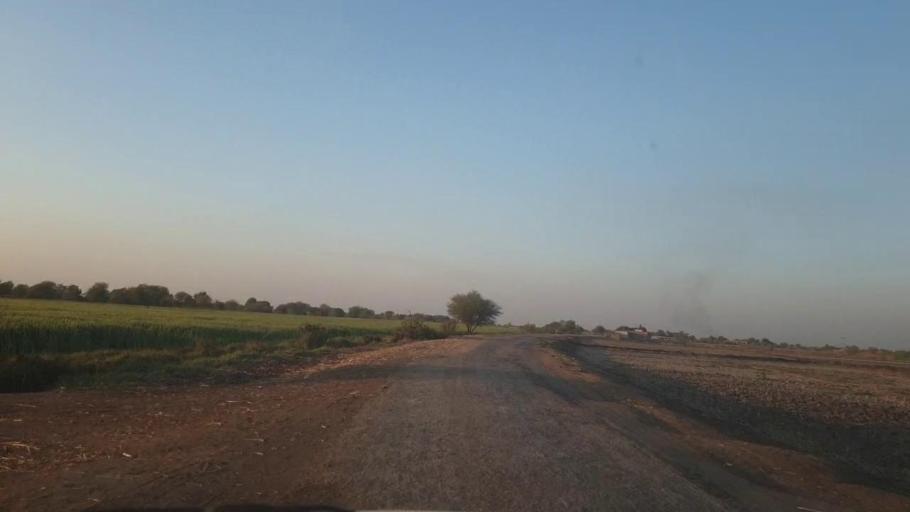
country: PK
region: Sindh
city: Mirpur Khas
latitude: 25.4659
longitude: 69.0700
